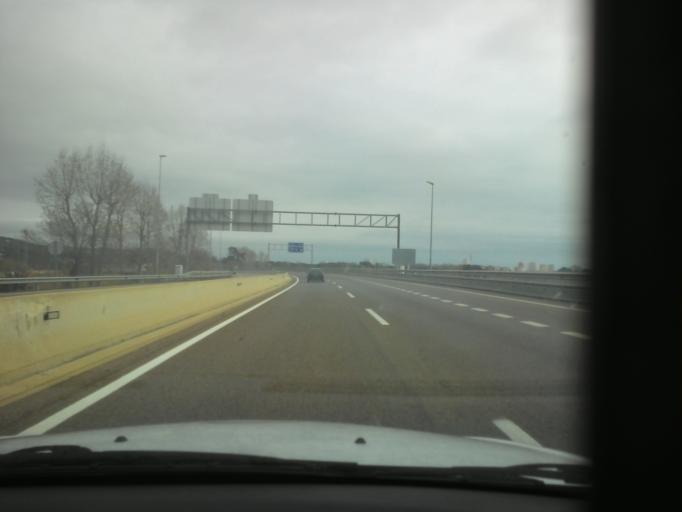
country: ES
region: Catalonia
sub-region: Provincia de Girona
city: Sant Feliu de Guixols
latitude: 41.8093
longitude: 3.0375
